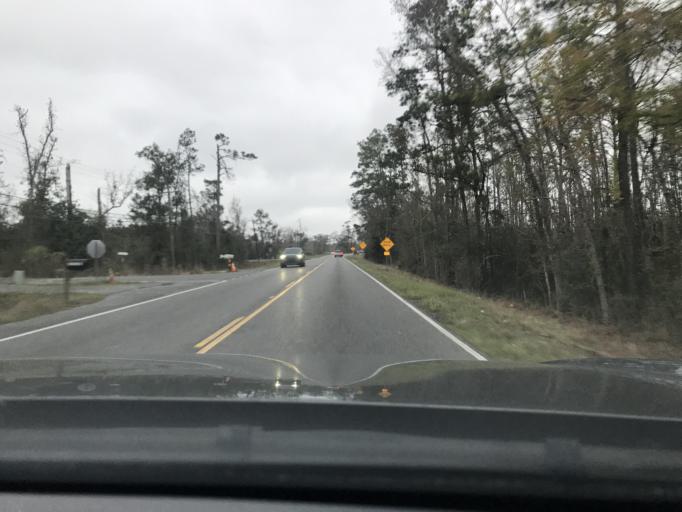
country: US
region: Louisiana
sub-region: Calcasieu Parish
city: Westlake
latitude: 30.2930
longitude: -93.2497
